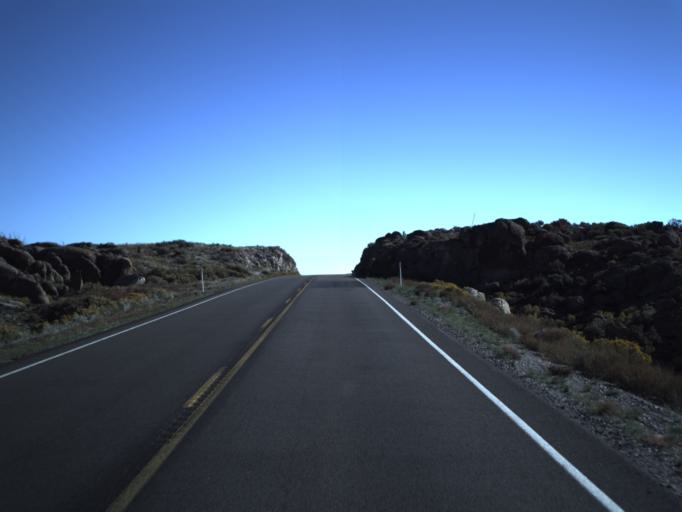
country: US
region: Utah
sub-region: Washington County
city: Enterprise
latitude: 37.7280
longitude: -114.0320
